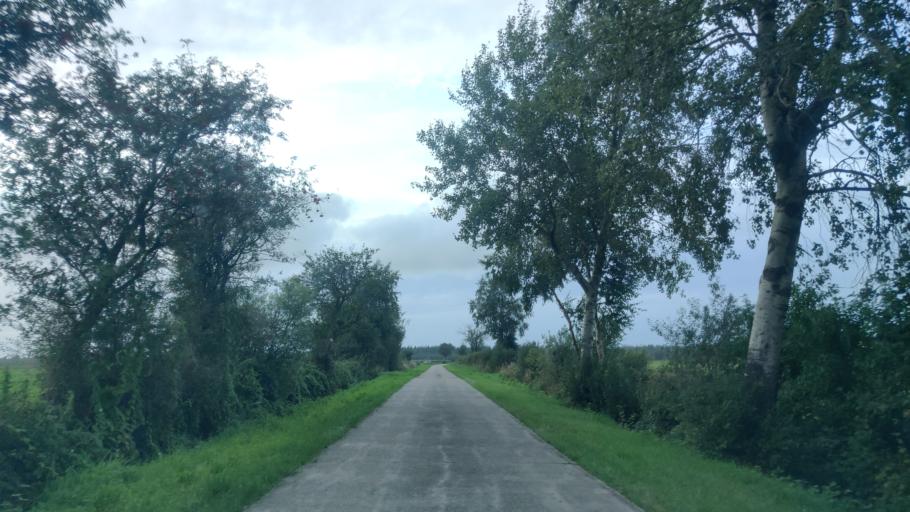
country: DE
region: Lower Saxony
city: Aurich
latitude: 53.5015
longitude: 7.4309
